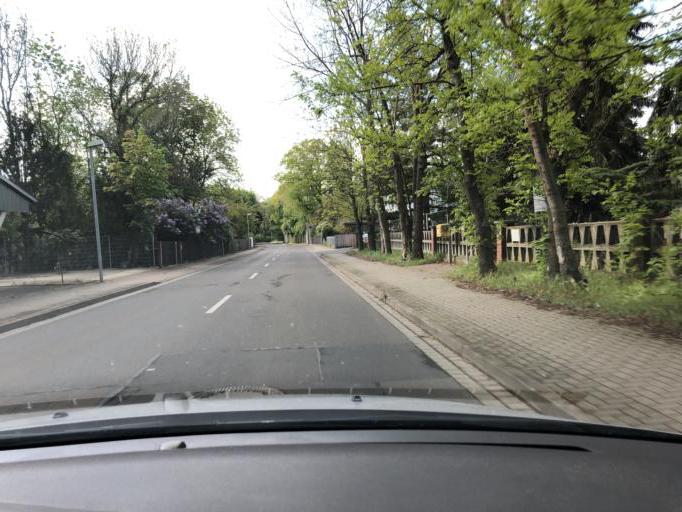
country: DE
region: Saxony
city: Markkleeberg
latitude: 51.2434
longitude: 12.3848
